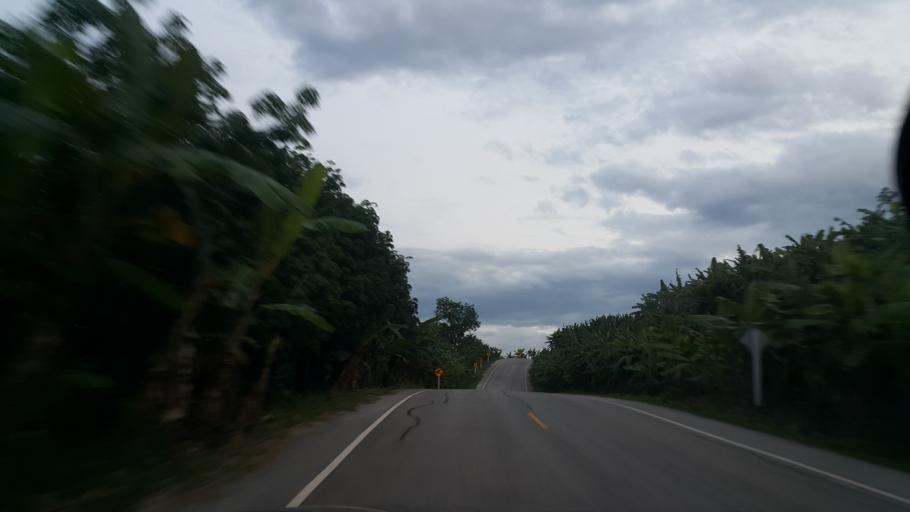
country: TH
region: Loei
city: Phu Ruea
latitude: 17.5253
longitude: 101.2316
